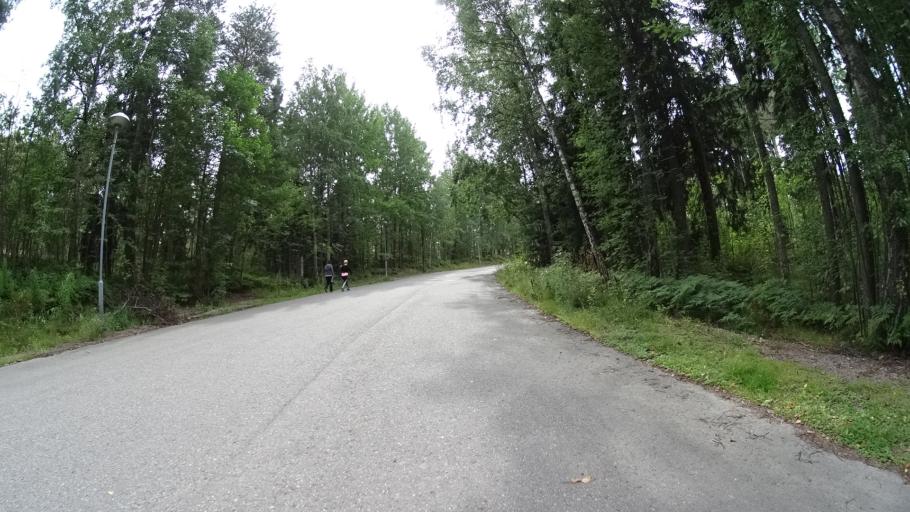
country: FI
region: Uusimaa
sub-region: Helsinki
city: Koukkuniemi
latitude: 60.1621
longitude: 24.7671
